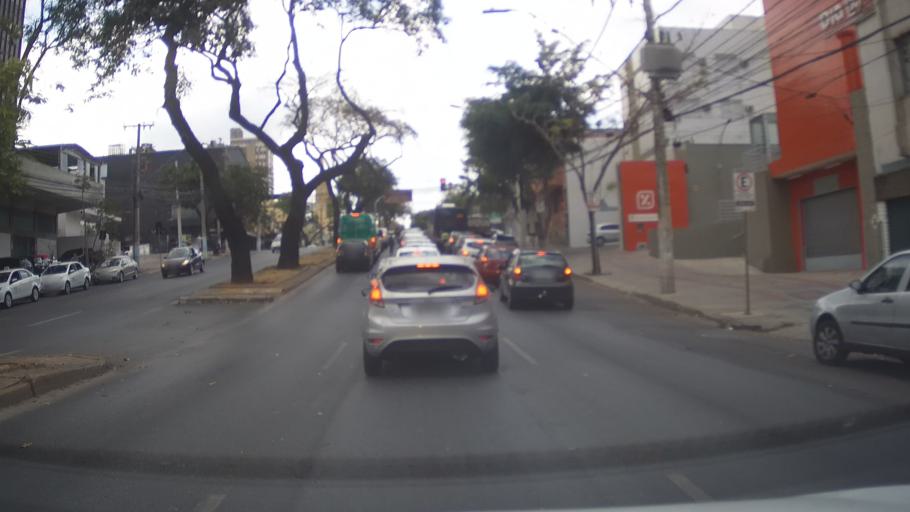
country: BR
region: Minas Gerais
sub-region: Belo Horizonte
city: Belo Horizonte
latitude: -19.9181
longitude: -43.9261
